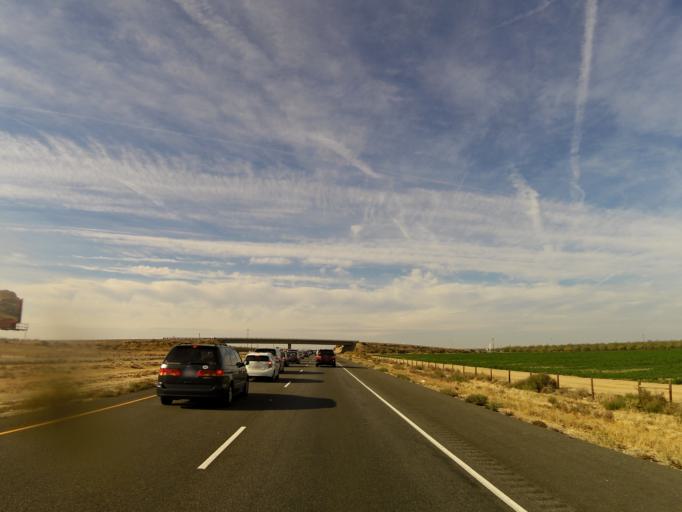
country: US
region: California
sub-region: Kern County
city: Buttonwillow
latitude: 35.4538
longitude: -119.4724
